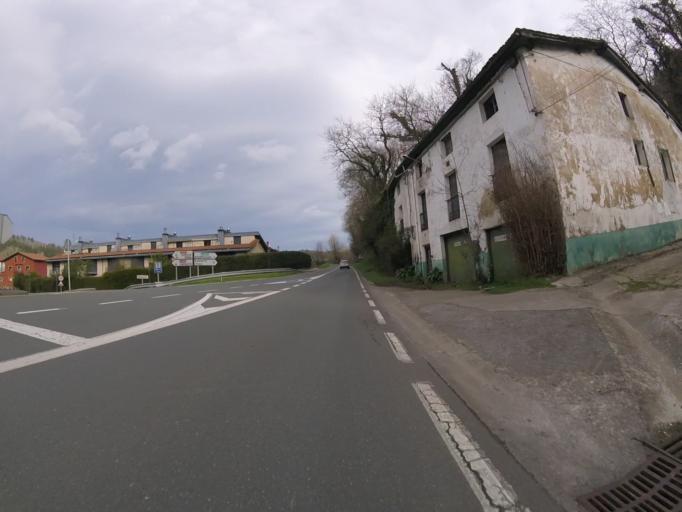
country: ES
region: Basque Country
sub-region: Provincia de Guipuzcoa
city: Cestona
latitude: 43.2539
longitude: -2.2597
